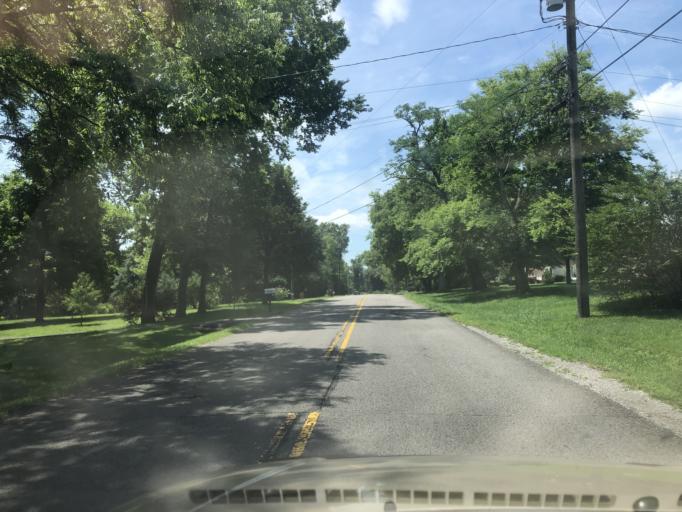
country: US
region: Tennessee
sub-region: Davidson County
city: Lakewood
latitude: 36.2506
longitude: -86.6919
